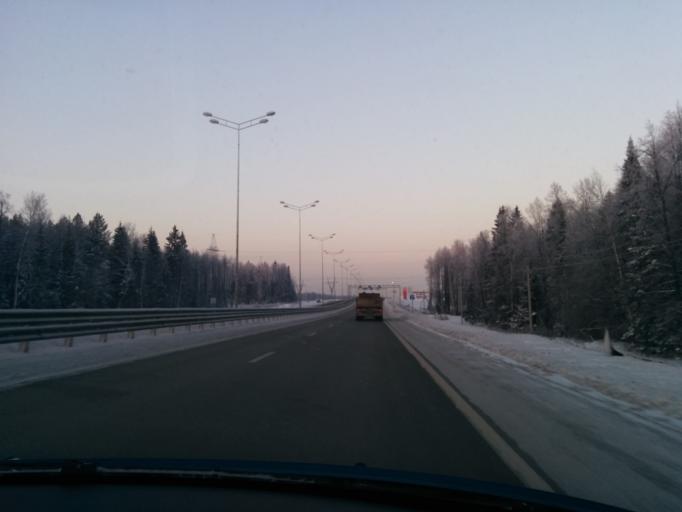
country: RU
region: Perm
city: Novyye Lyady
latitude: 58.0372
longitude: 56.4336
